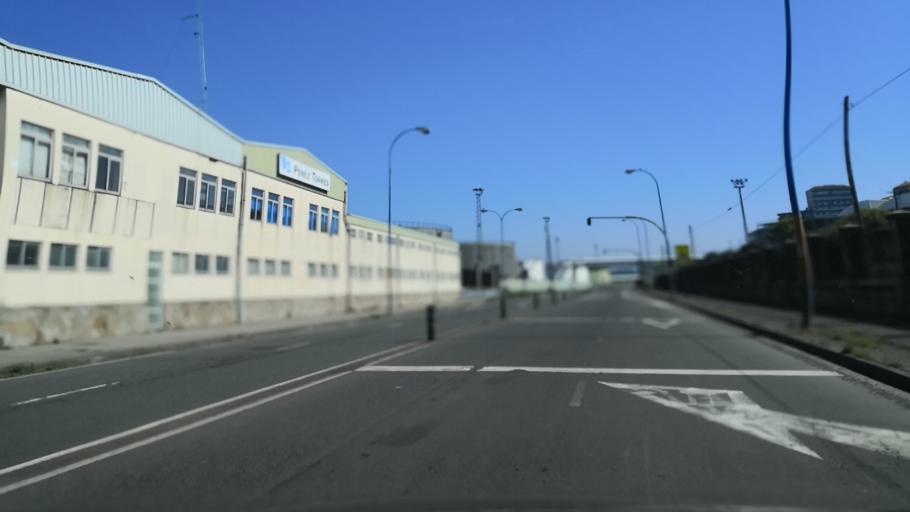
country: ES
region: Galicia
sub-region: Provincia da Coruna
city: A Coruna
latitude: 43.3561
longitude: -8.3923
